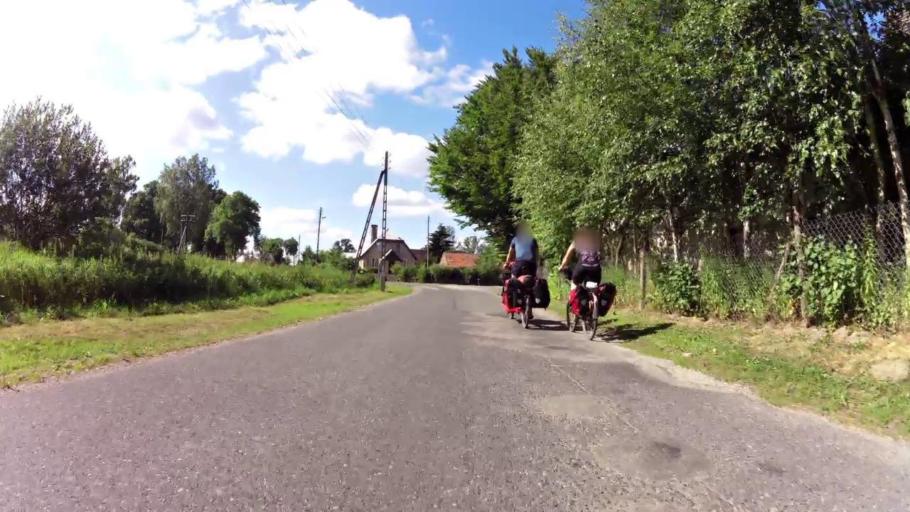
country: PL
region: West Pomeranian Voivodeship
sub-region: Powiat lobeski
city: Lobez
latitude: 53.6415
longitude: 15.6745
